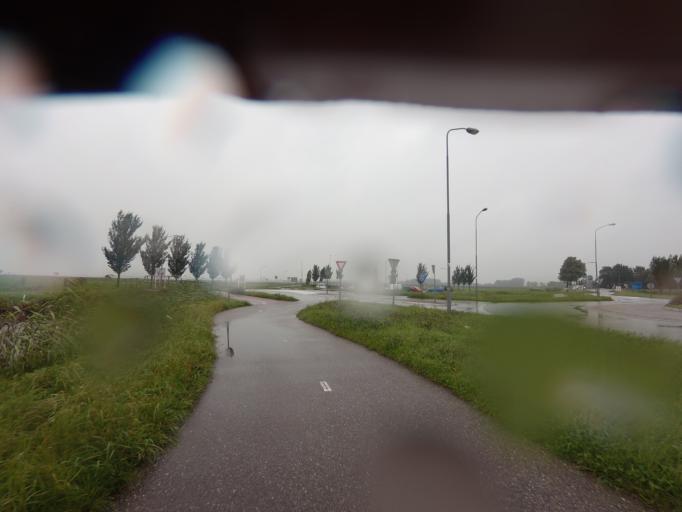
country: NL
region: North Holland
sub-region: Gemeente Medemblik
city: Opperdoes
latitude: 52.7200
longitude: 5.0233
